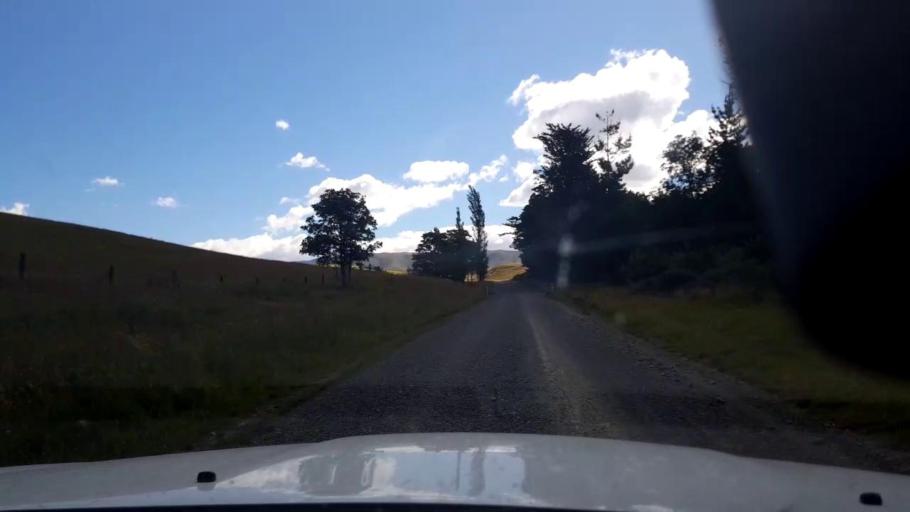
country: NZ
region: Canterbury
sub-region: Timaru District
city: Pleasant Point
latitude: -44.3109
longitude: 170.9061
